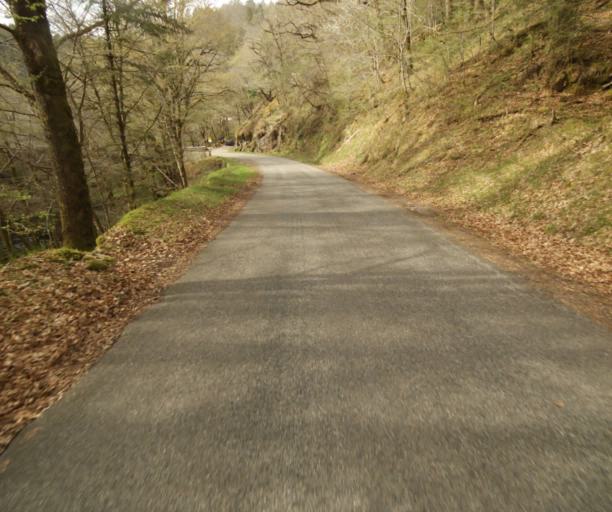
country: FR
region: Limousin
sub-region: Departement de la Correze
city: Argentat
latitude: 45.1980
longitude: 1.9767
